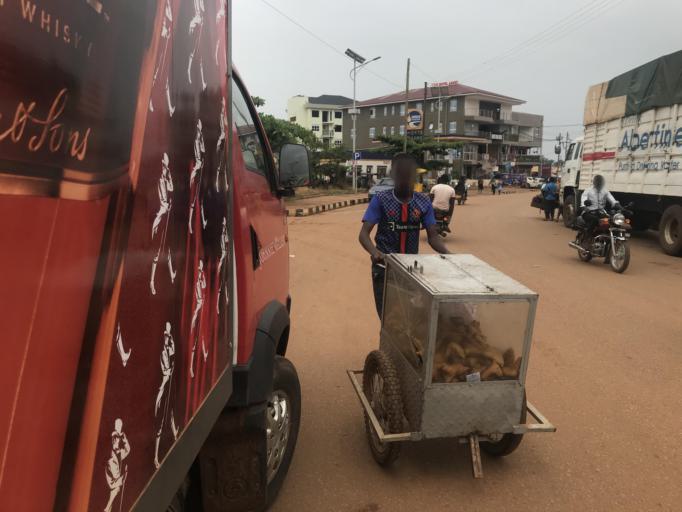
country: UG
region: Western Region
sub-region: Hoima District
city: Hoima
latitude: 1.4326
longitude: 31.3504
